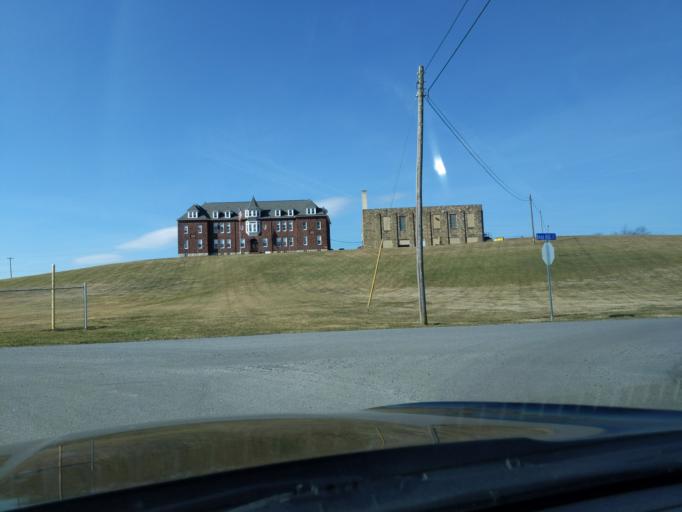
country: US
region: Pennsylvania
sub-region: Blair County
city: Martinsburg
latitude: 40.3089
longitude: -78.3394
